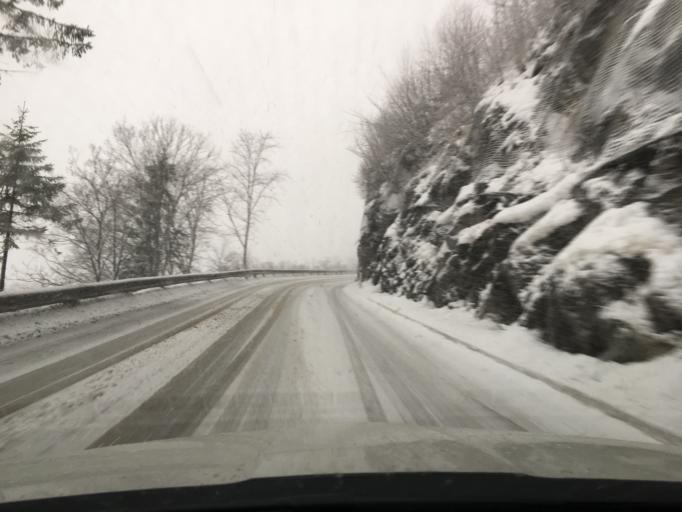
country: AT
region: Tyrol
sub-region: Politischer Bezirk Schwaz
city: Mayrhofen
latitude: 47.1610
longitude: 11.8435
